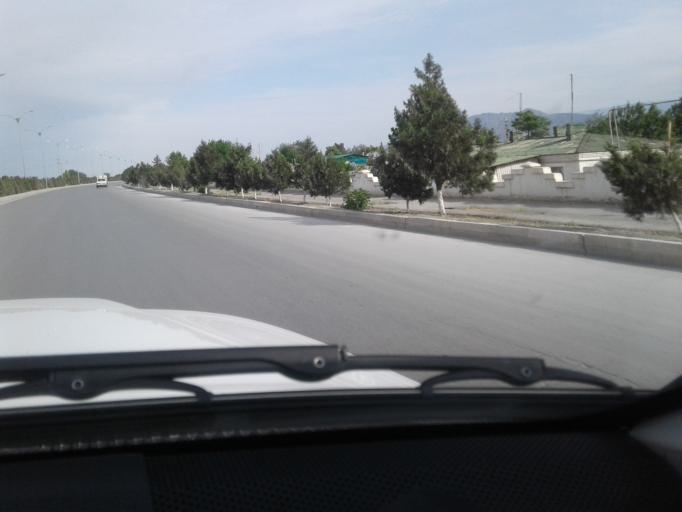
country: TM
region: Ahal
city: Abadan
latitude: 38.1558
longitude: 57.9728
